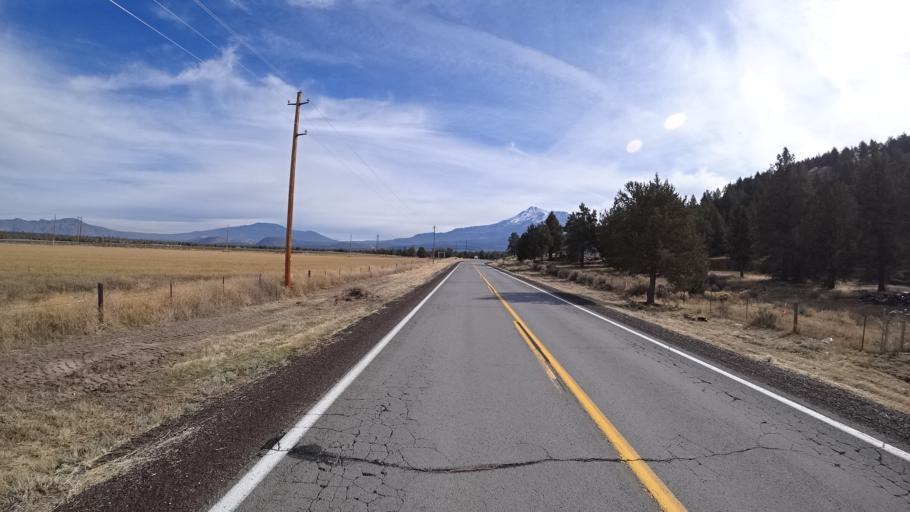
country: US
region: California
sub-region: Siskiyou County
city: Weed
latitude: 41.5422
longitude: -122.3679
